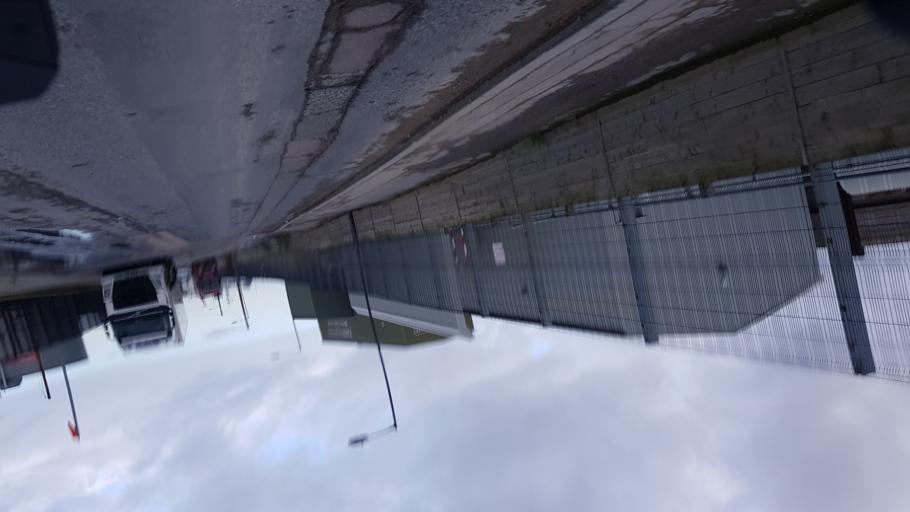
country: GB
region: England
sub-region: Greater London
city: Blackheath
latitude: 51.4919
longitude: 0.0247
